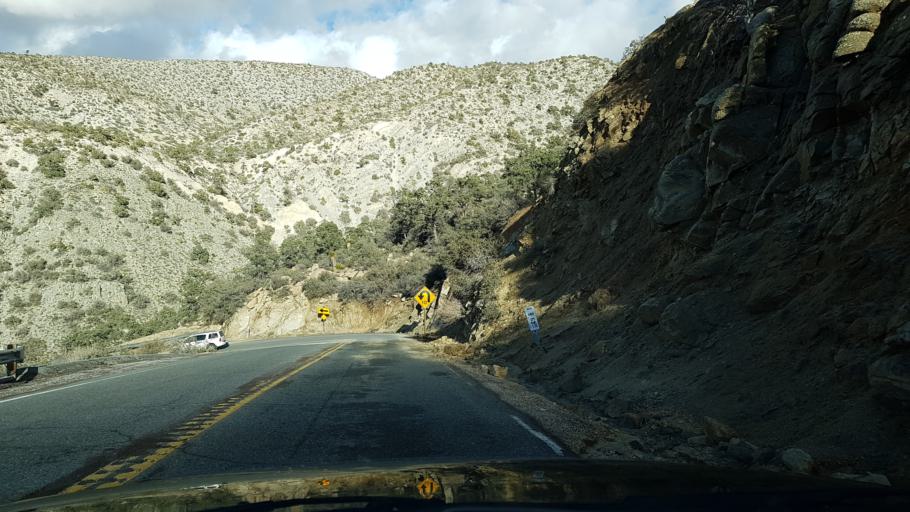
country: US
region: California
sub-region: San Bernardino County
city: Big Bear City
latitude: 34.3319
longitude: -116.8298
